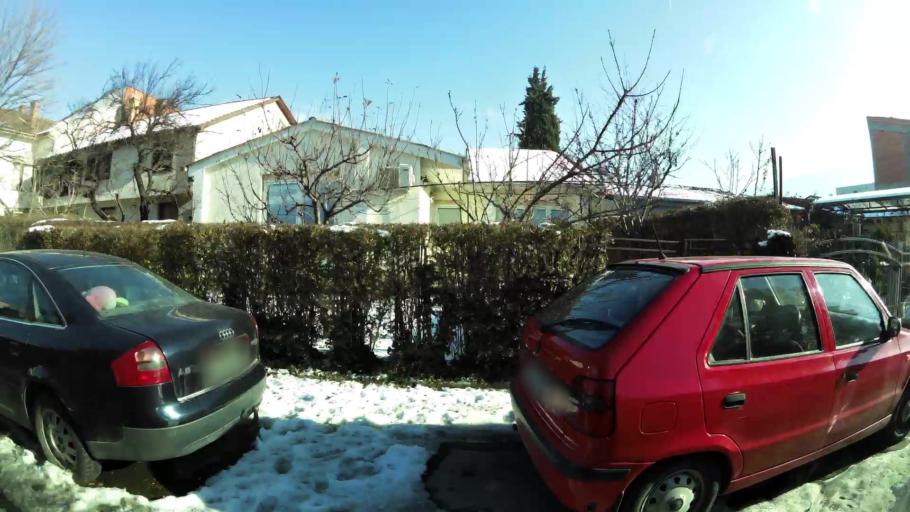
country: MK
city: Krushopek
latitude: 42.0054
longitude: 21.3772
